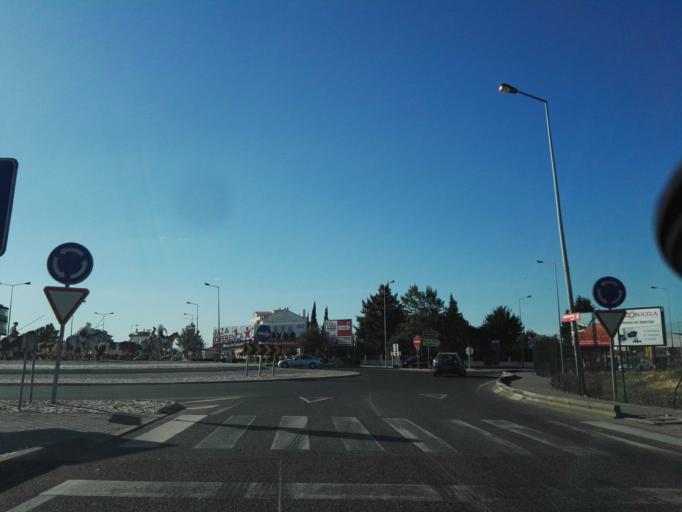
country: PT
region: Santarem
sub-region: Benavente
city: Samora Correia
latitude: 38.9215
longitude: -8.8812
